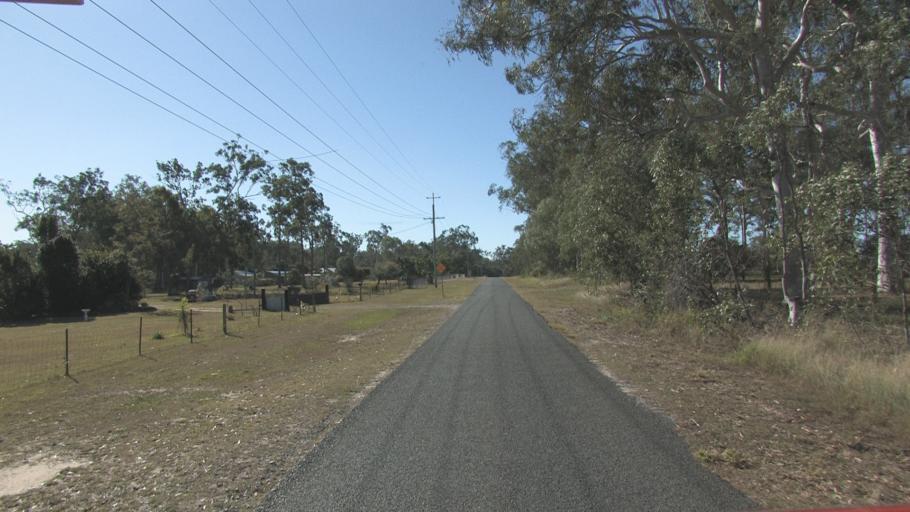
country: AU
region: Queensland
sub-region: Logan
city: Logan Reserve
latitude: -27.7325
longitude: 153.0779
